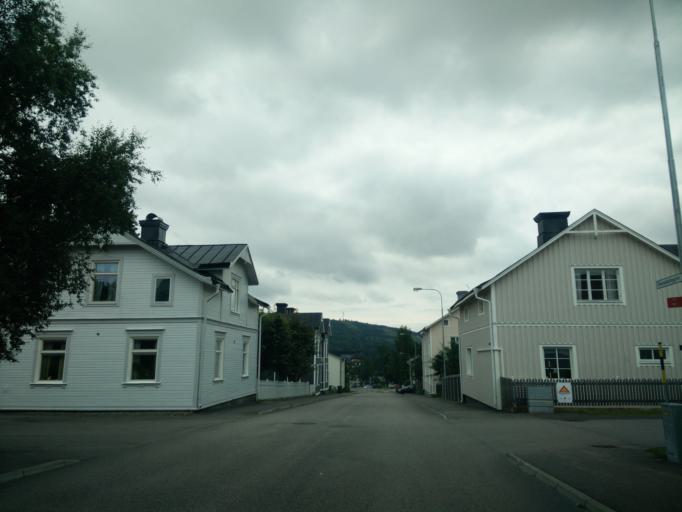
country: SE
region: Vaesternorrland
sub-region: Haernoesands Kommun
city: Haernoesand
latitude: 62.6269
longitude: 17.9253
